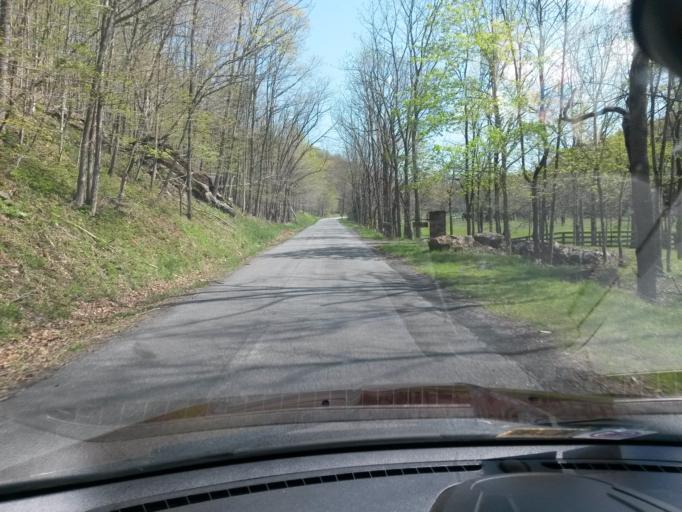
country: US
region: Virginia
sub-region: Highland County
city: Monterey
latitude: 38.2212
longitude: -79.6683
